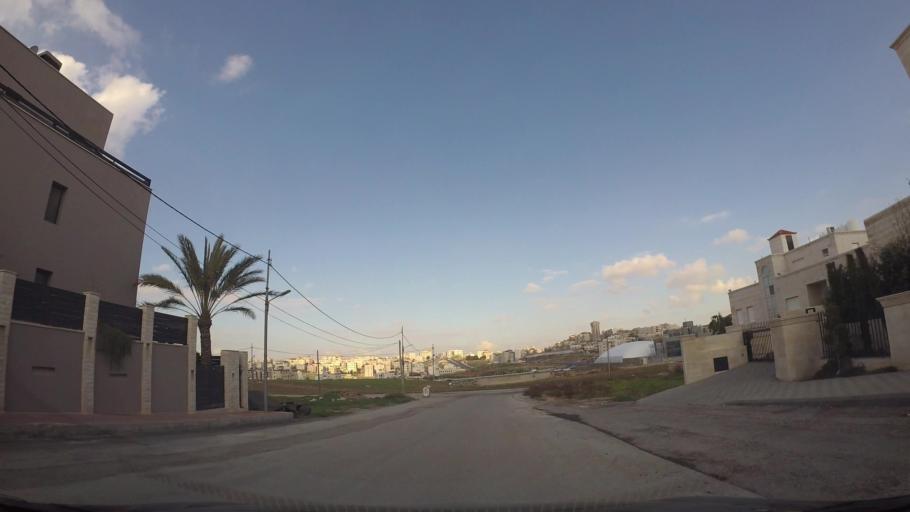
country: JO
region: Amman
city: Al Bunayyat ash Shamaliyah
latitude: 31.9114
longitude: 35.8770
